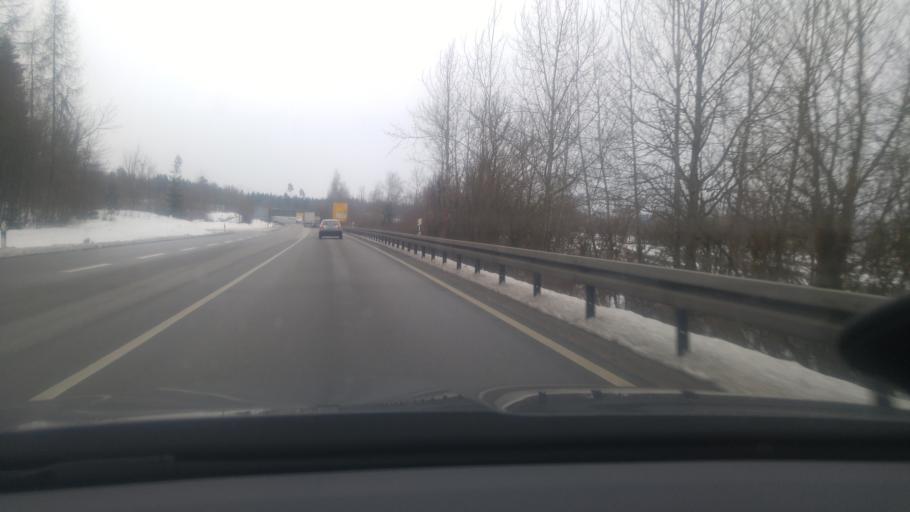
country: DE
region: Baden-Wuerttemberg
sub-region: Freiburg Region
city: Bad Durrheim
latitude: 48.0484
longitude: 8.5417
